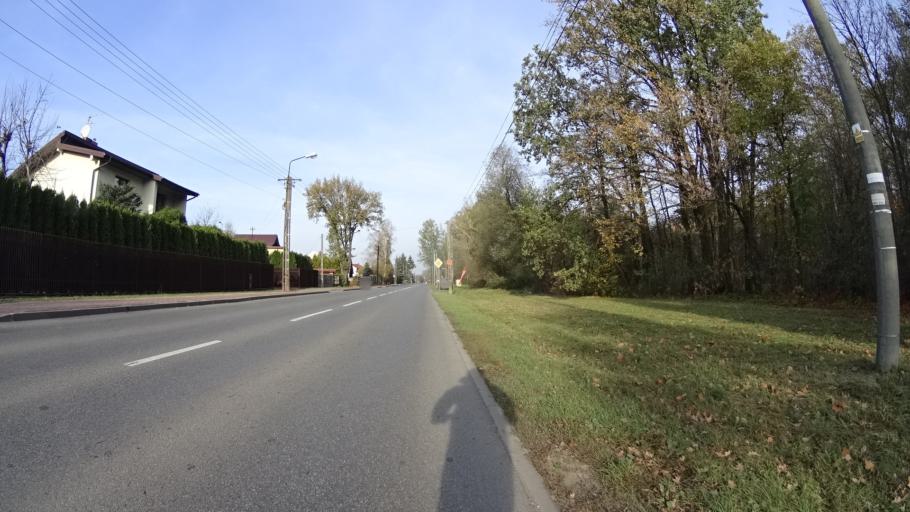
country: PL
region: Masovian Voivodeship
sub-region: Powiat warszawski zachodni
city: Babice
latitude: 52.2554
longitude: 20.8494
